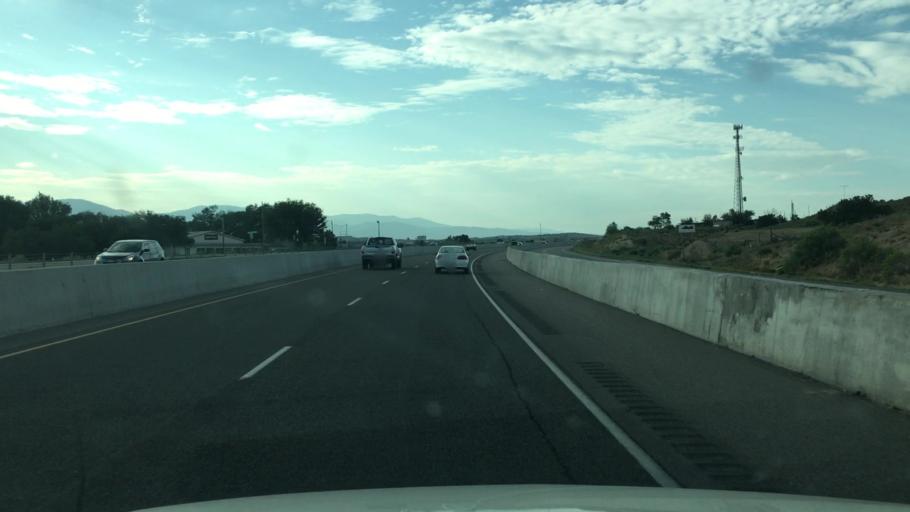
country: US
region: New Mexico
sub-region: Santa Fe County
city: El Valle de Arroyo Seco
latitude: 35.9580
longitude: -106.0238
